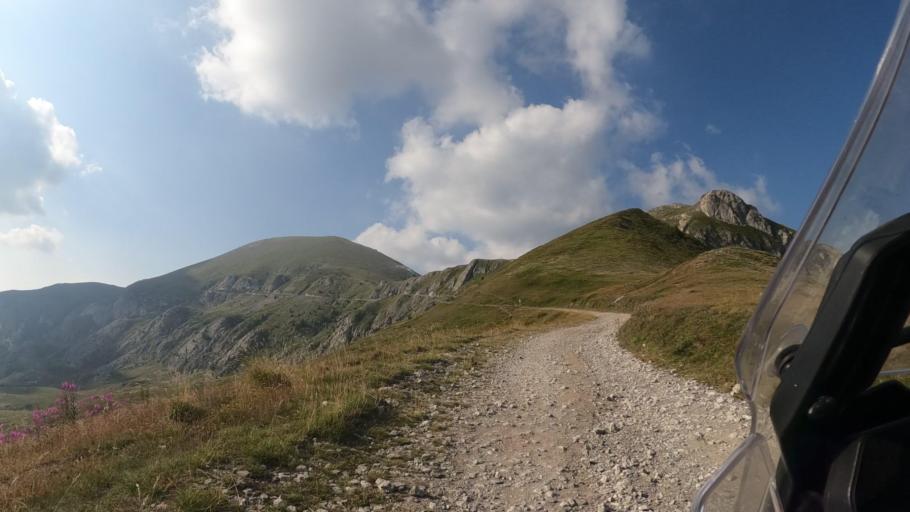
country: IT
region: Piedmont
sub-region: Provincia di Cuneo
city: Limone Piemonte
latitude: 44.1577
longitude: 7.6712
